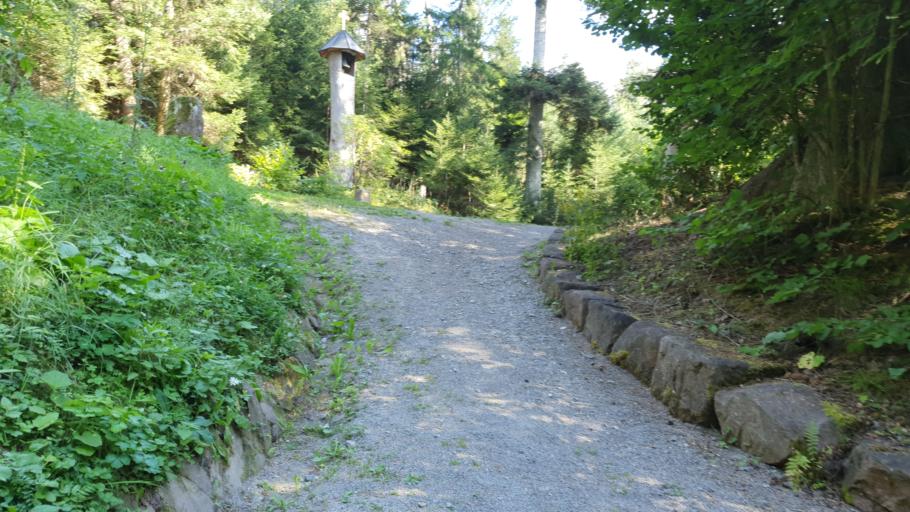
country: DE
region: Baden-Wuerttemberg
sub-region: Karlsruhe Region
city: Pfalzgrafenweiler
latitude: 48.5428
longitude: 8.5577
